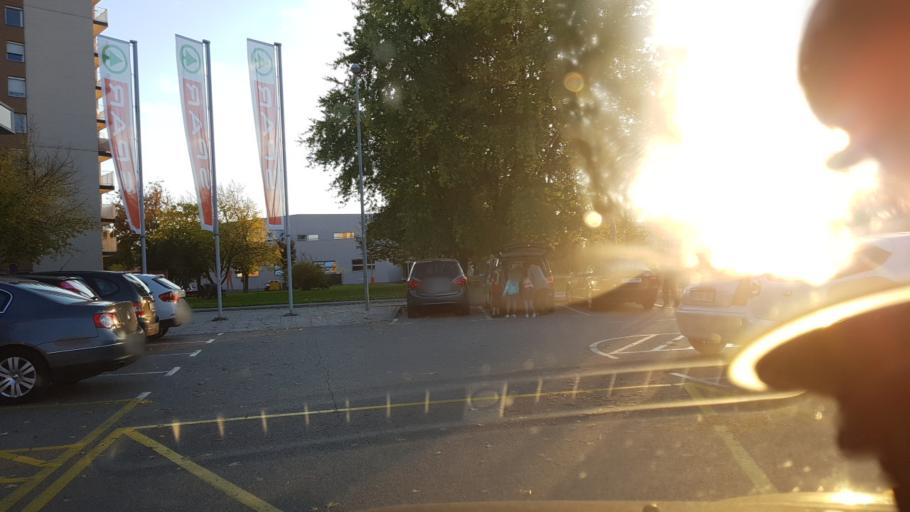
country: SI
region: Brezice
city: Brezice
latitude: 45.9088
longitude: 15.5970
